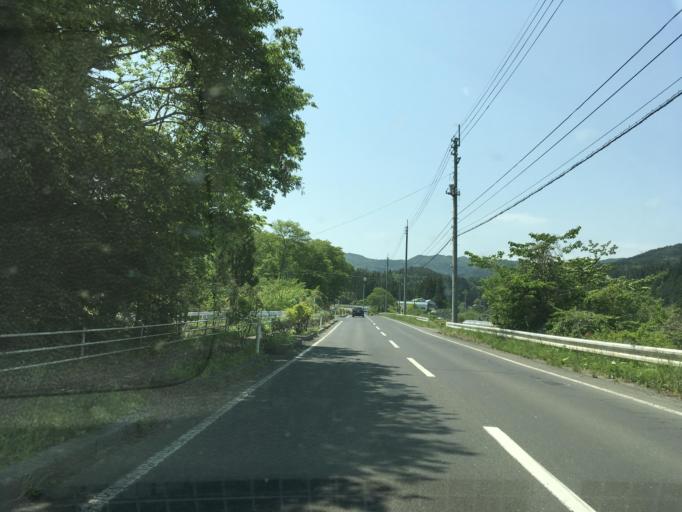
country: JP
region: Iwate
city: Ofunato
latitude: 38.8671
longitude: 141.5342
